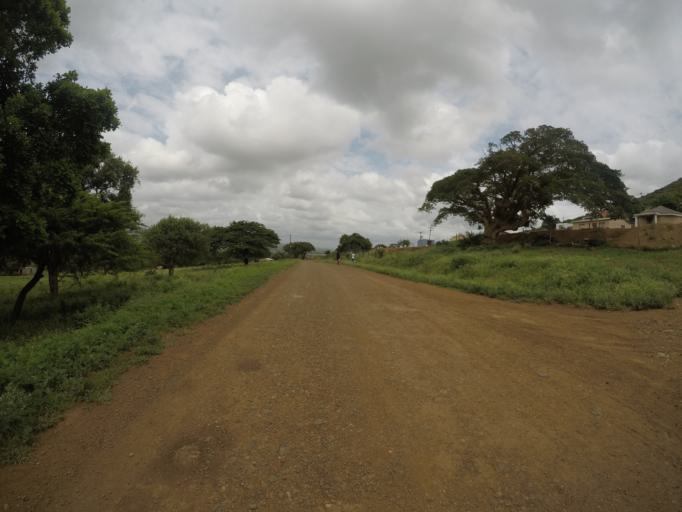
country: ZA
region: KwaZulu-Natal
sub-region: uThungulu District Municipality
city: Empangeni
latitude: -28.5928
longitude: 31.8822
